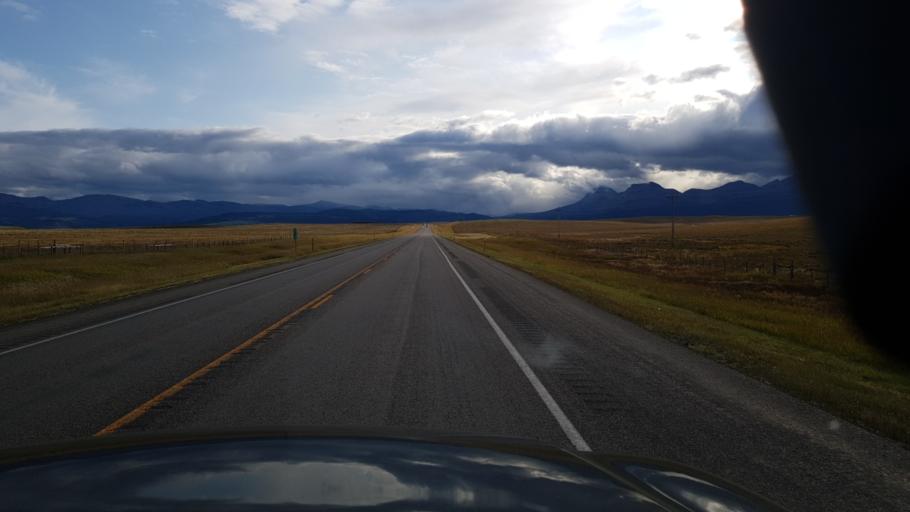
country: US
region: Montana
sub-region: Glacier County
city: South Browning
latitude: 48.4805
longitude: -113.1391
